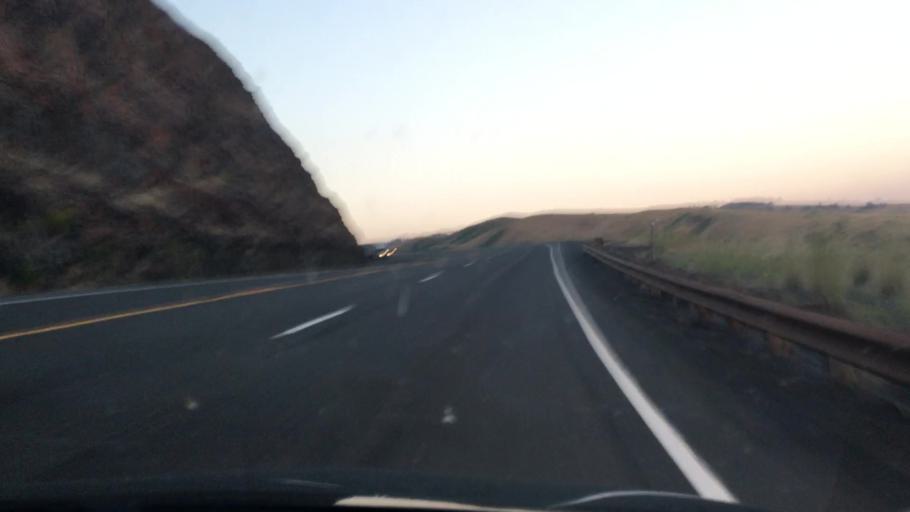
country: US
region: Idaho
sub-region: Idaho County
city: Grangeville
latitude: 45.8205
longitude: -116.2696
